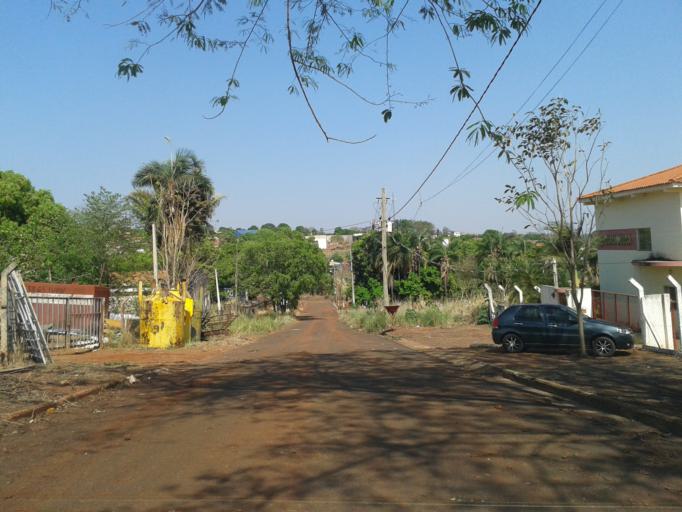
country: BR
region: Minas Gerais
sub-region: Ituiutaba
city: Ituiutaba
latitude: -18.9493
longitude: -49.4547
